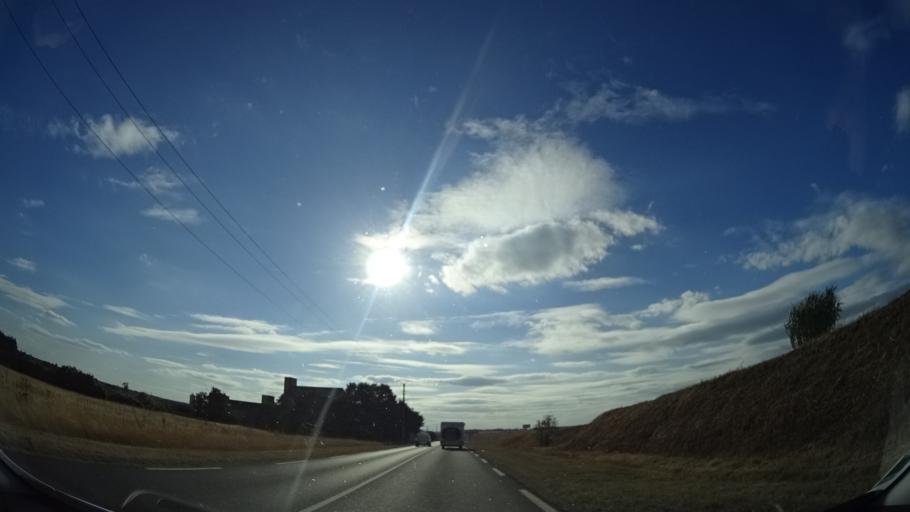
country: FR
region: Centre
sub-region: Departement du Loir-et-Cher
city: Oucques
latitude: 47.9043
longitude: 1.3818
